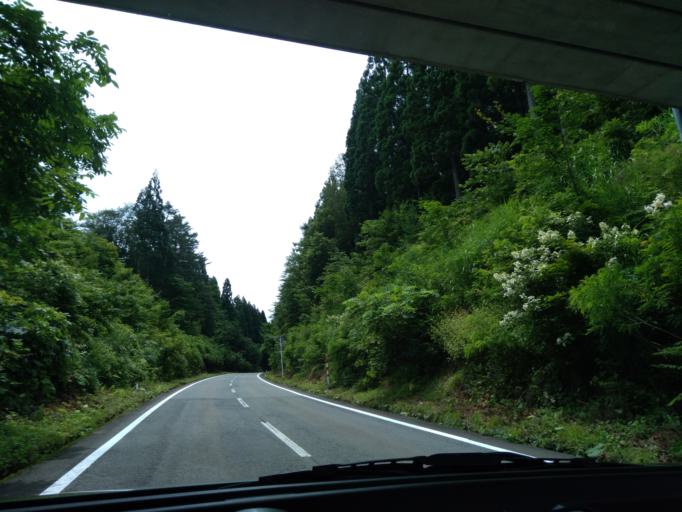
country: JP
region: Akita
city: Kakunodatemachi
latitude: 39.5682
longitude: 140.6370
